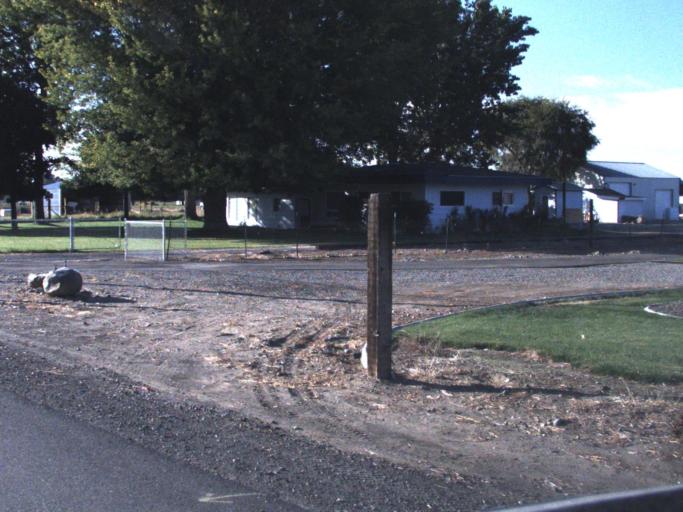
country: US
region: Washington
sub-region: Walla Walla County
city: Burbank
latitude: 46.2117
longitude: -118.9970
